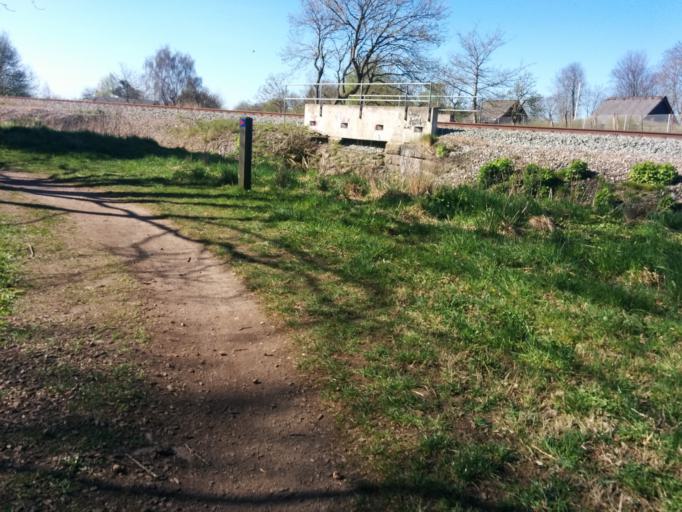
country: DK
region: North Denmark
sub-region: Alborg Kommune
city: Aalborg
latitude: 57.0191
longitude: 9.9129
